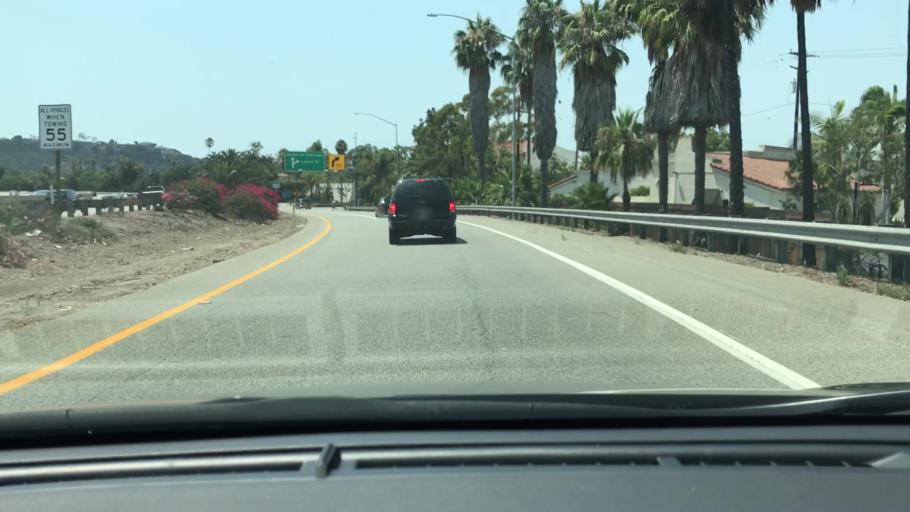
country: US
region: California
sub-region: Santa Barbara County
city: Santa Barbara
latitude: 34.4198
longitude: -119.6867
